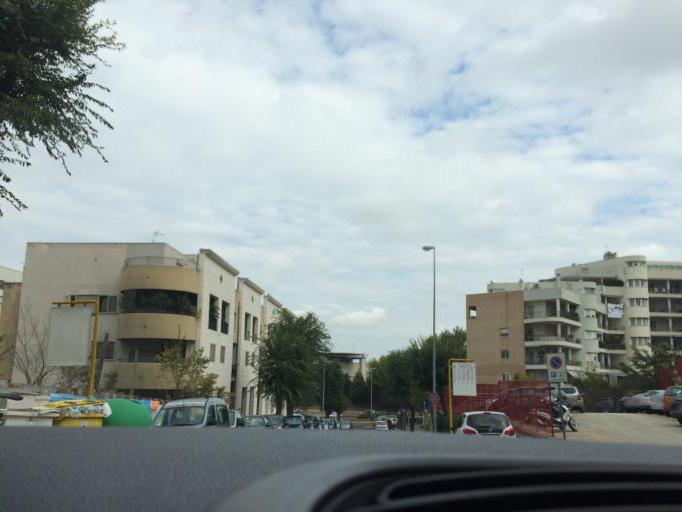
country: IT
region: Basilicate
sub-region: Provincia di Matera
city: Matera
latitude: 40.6697
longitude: 16.5959
